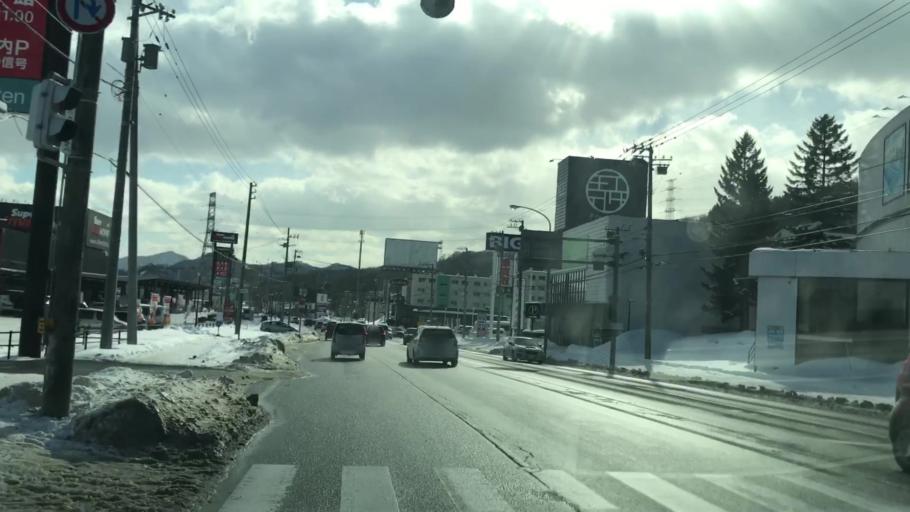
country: JP
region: Hokkaido
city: Sapporo
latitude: 43.1013
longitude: 141.2530
